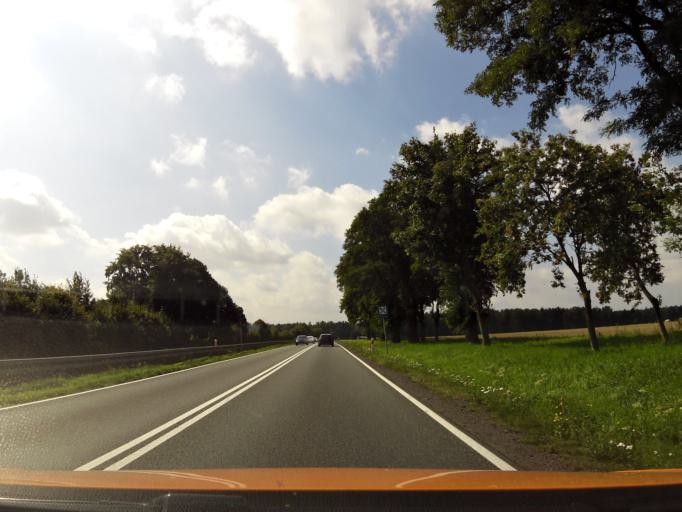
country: PL
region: West Pomeranian Voivodeship
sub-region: Powiat goleniowski
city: Nowogard
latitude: 53.7023
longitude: 15.1692
